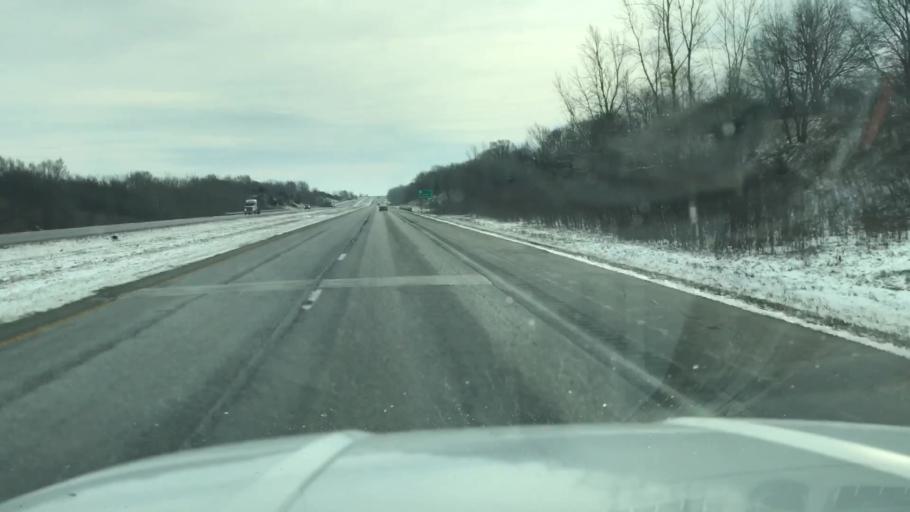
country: US
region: Missouri
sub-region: Holt County
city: Oregon
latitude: 40.0382
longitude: -95.1261
